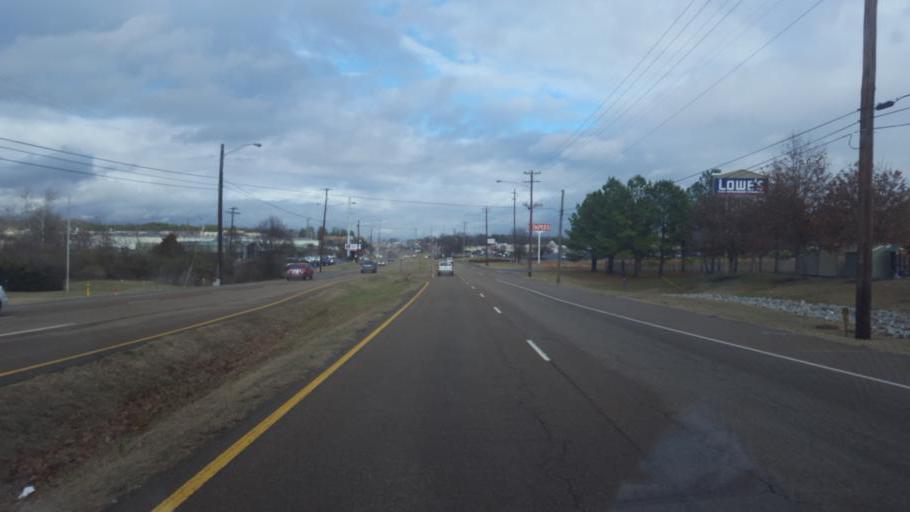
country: US
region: Tennessee
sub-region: McMinn County
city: Athens
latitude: 35.4469
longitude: -84.6281
